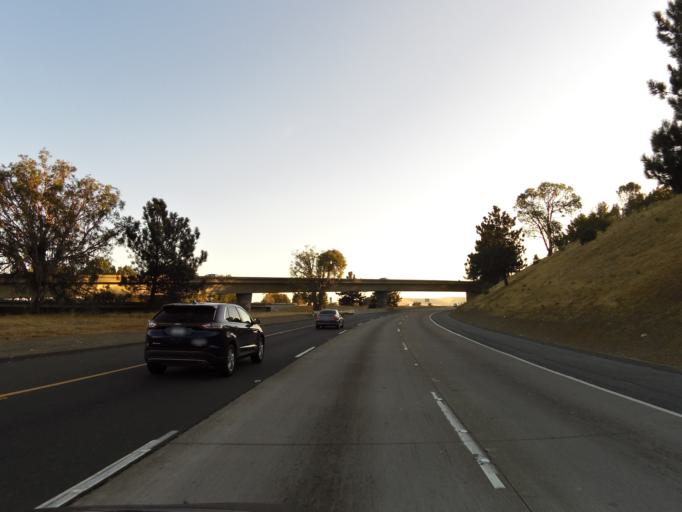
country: US
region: California
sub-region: Contra Costa County
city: Concord
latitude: 38.0048
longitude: -122.0364
